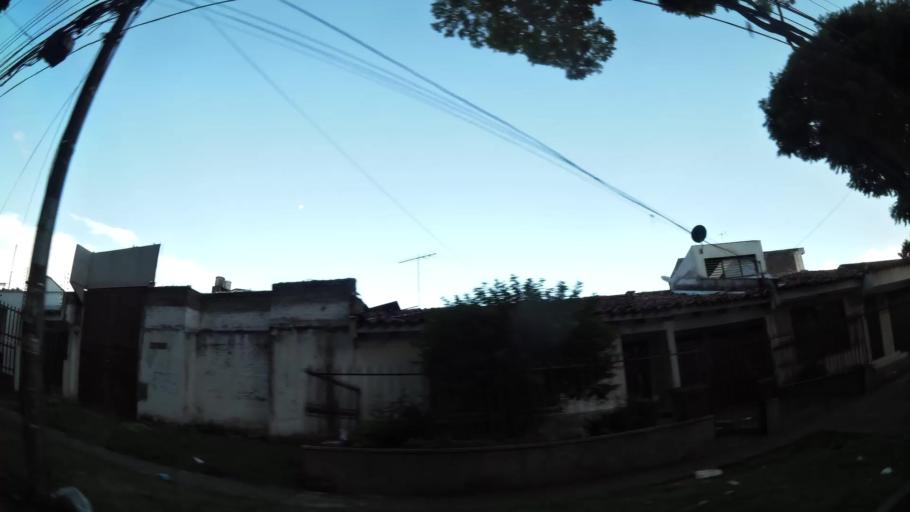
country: CO
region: Valle del Cauca
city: Cali
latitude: 3.4070
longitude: -76.5497
